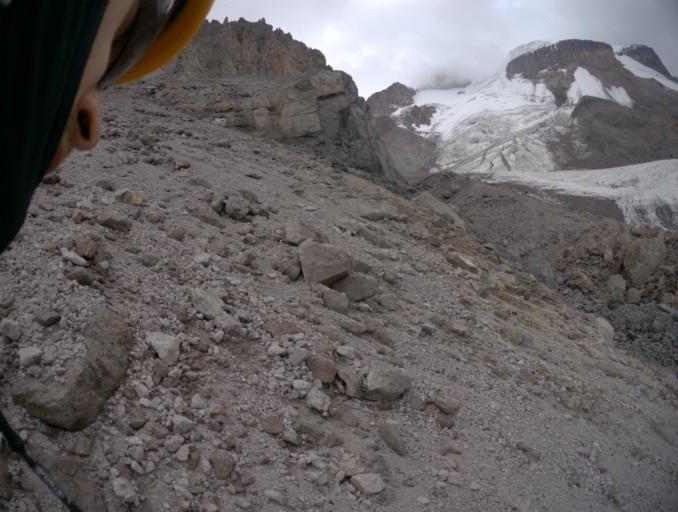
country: RU
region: Kabardino-Balkariya
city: Terskol
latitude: 43.3810
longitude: 42.3948
